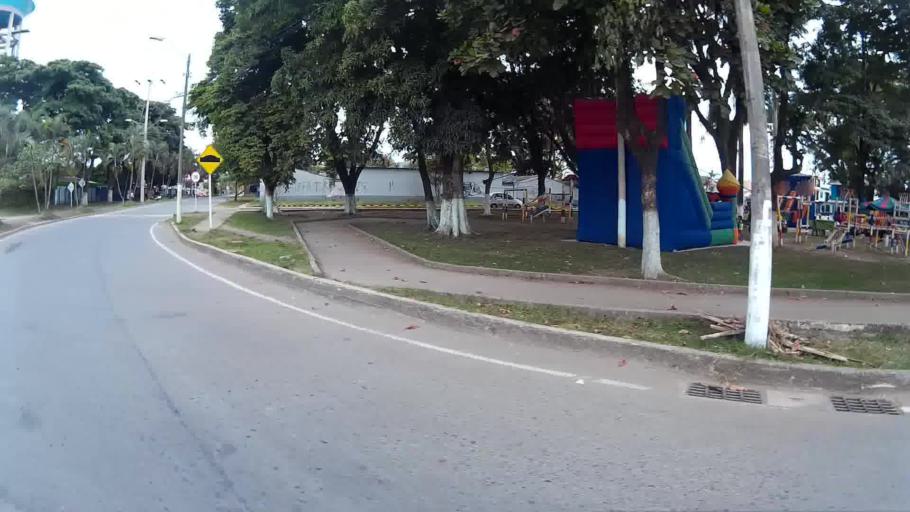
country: CO
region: Risaralda
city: La Virginia
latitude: 4.9018
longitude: -75.8842
